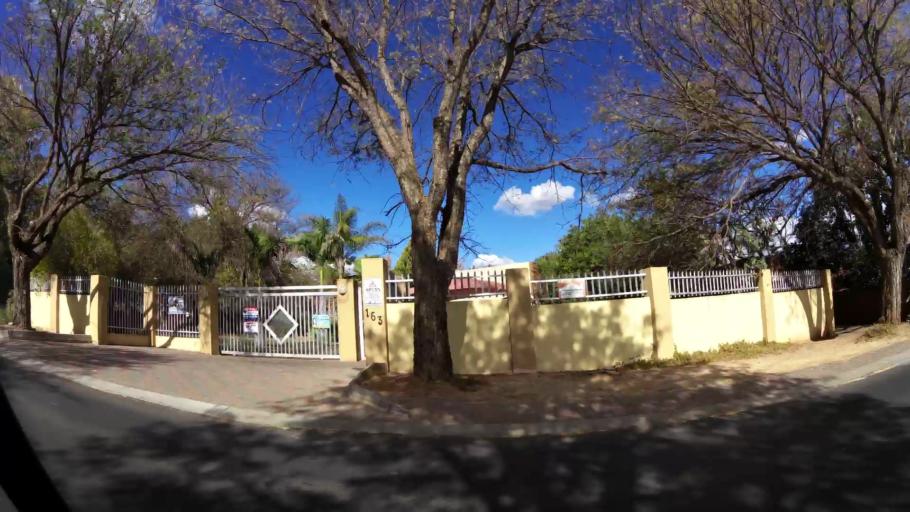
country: ZA
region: Limpopo
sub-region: Capricorn District Municipality
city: Polokwane
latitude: -23.8886
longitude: 29.4794
